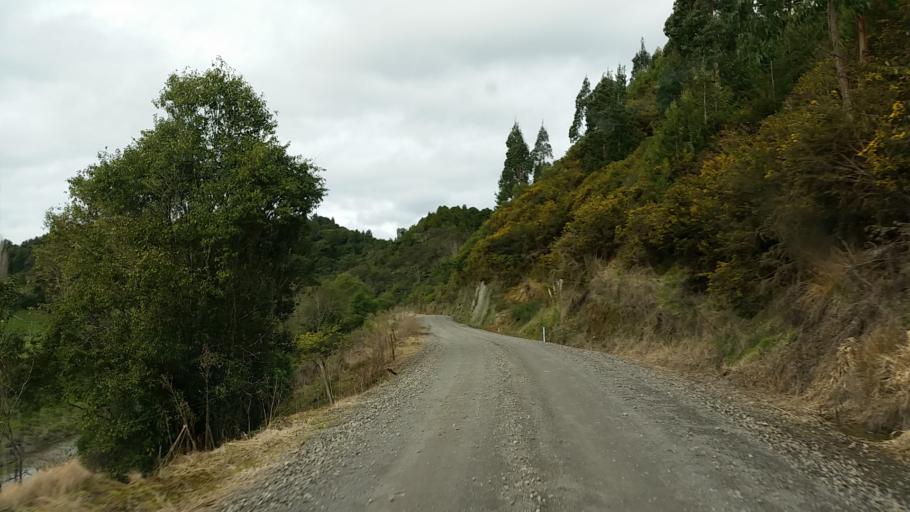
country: NZ
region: Taranaki
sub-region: New Plymouth District
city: Waitara
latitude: -39.1567
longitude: 174.5258
